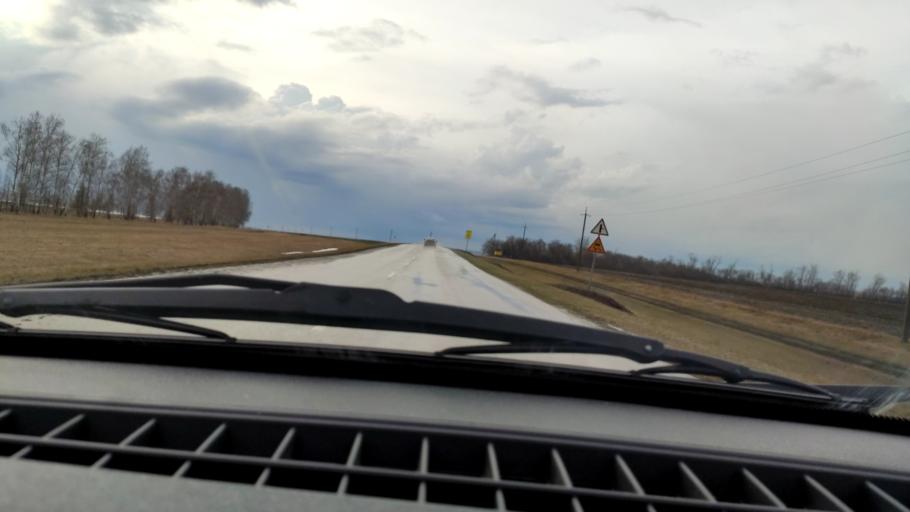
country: RU
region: Bashkortostan
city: Kushnarenkovo
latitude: 55.1027
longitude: 55.0342
